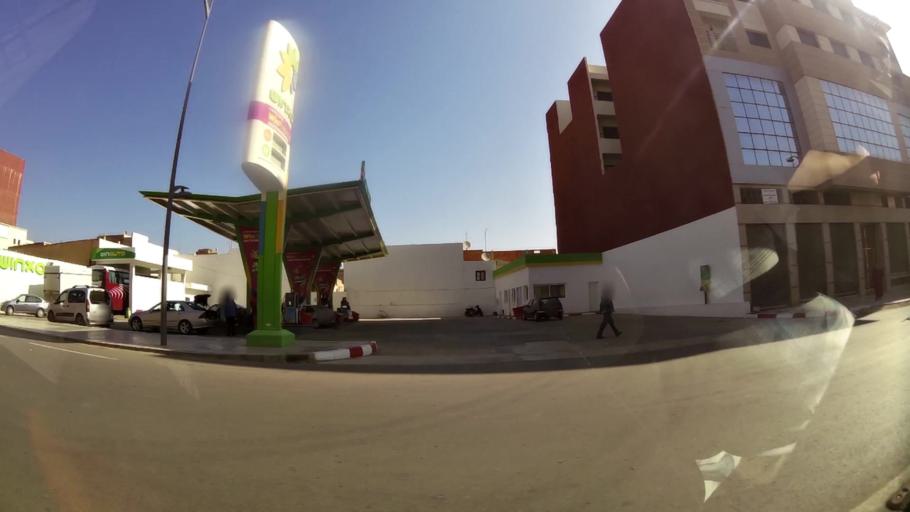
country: MA
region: Oriental
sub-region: Oujda-Angad
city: Oujda
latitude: 34.6802
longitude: -1.9331
